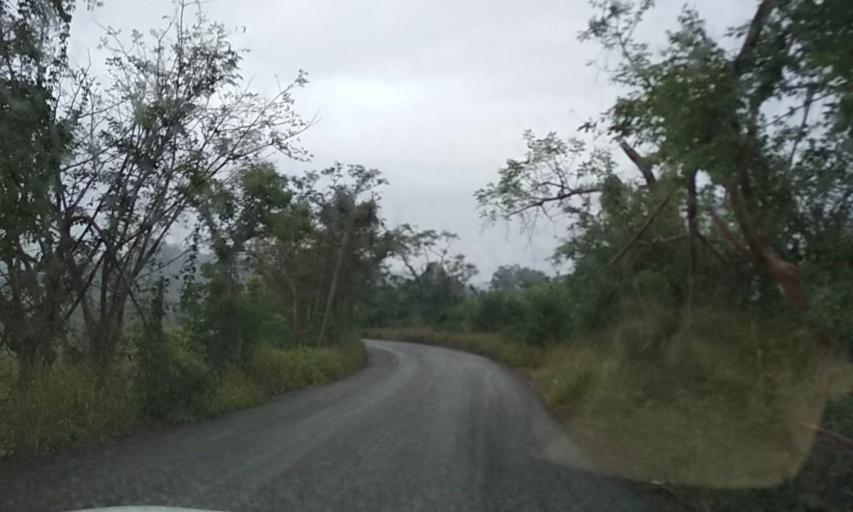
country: MX
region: Veracruz
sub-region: Coatzintla
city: Manuel Maria Contreras
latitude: 20.4548
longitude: -97.4740
